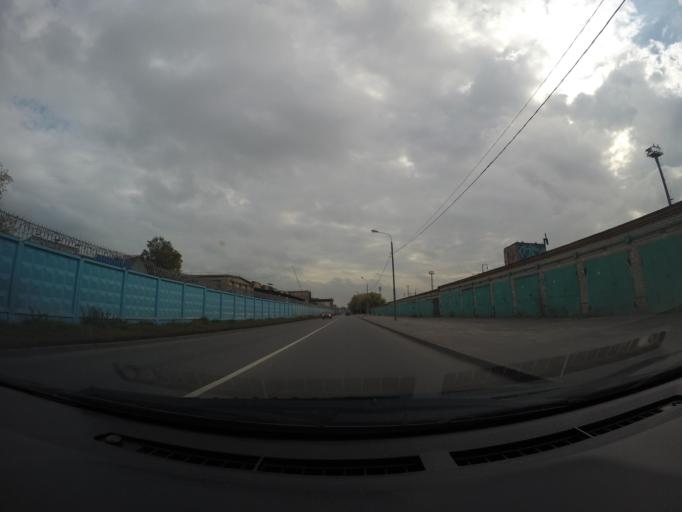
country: RU
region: Moscow
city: Lefortovo
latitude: 55.7706
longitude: 37.7189
